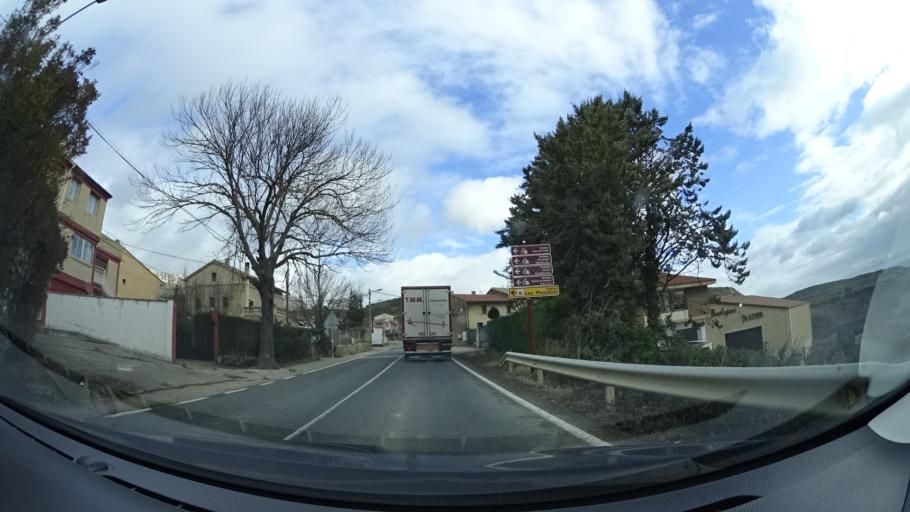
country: ES
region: La Rioja
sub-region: Provincia de La Rioja
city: Abalos
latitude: 42.5709
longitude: -2.7110
